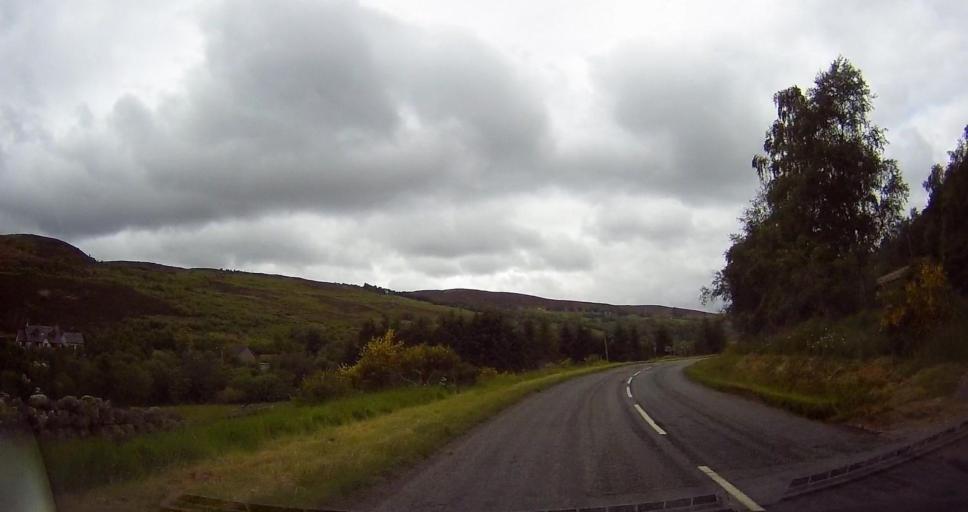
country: GB
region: Scotland
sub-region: Highland
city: Dornoch
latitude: 58.0034
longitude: -4.1879
